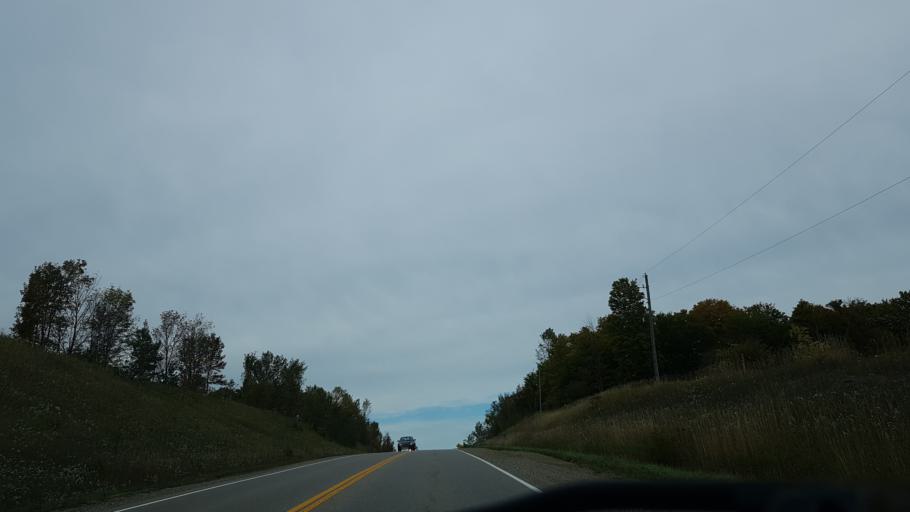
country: CA
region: Ontario
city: Orangeville
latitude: 44.0565
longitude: -80.0129
